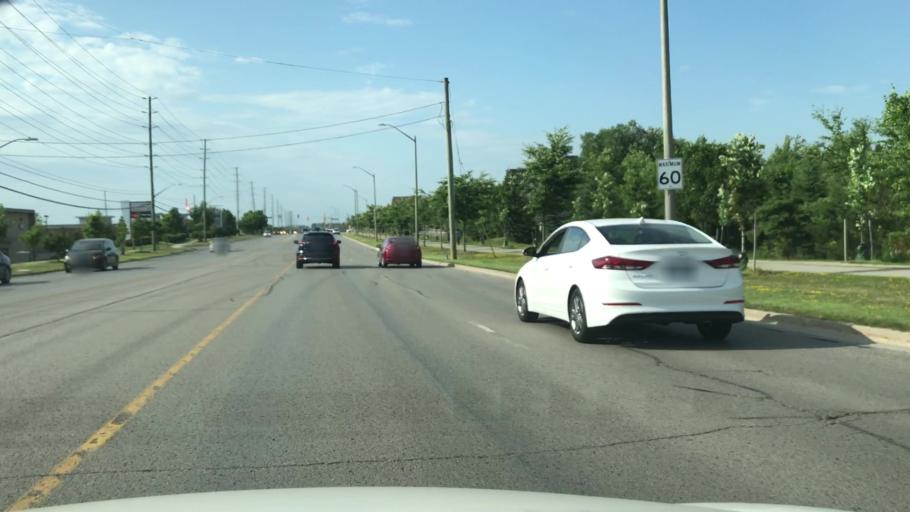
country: CA
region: Ontario
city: Newmarket
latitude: 44.0163
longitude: -79.4463
